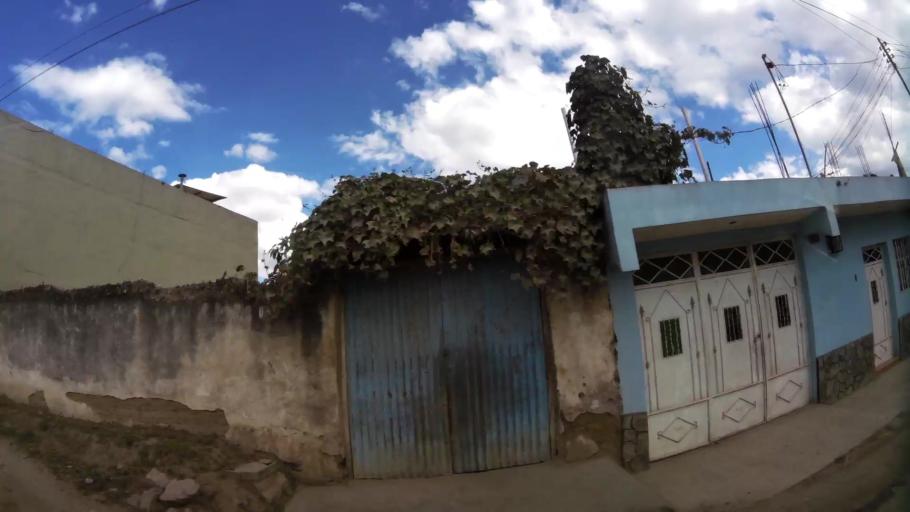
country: GT
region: Quetzaltenango
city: Quetzaltenango
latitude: 14.8396
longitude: -91.5423
